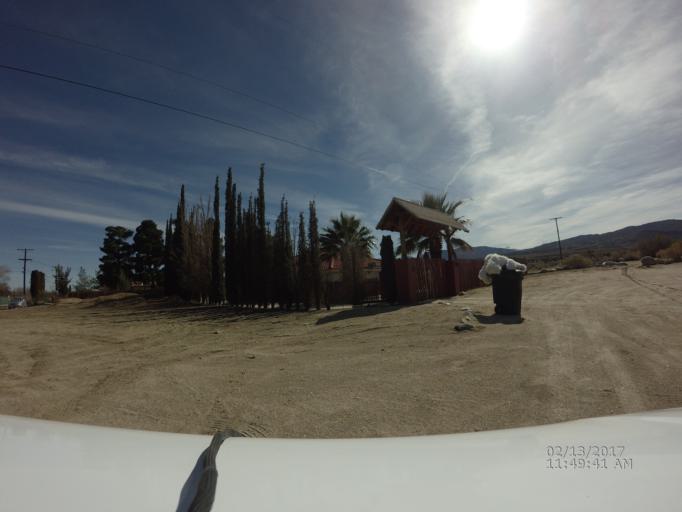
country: US
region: California
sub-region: Los Angeles County
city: Littlerock
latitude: 34.5190
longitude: -117.9881
